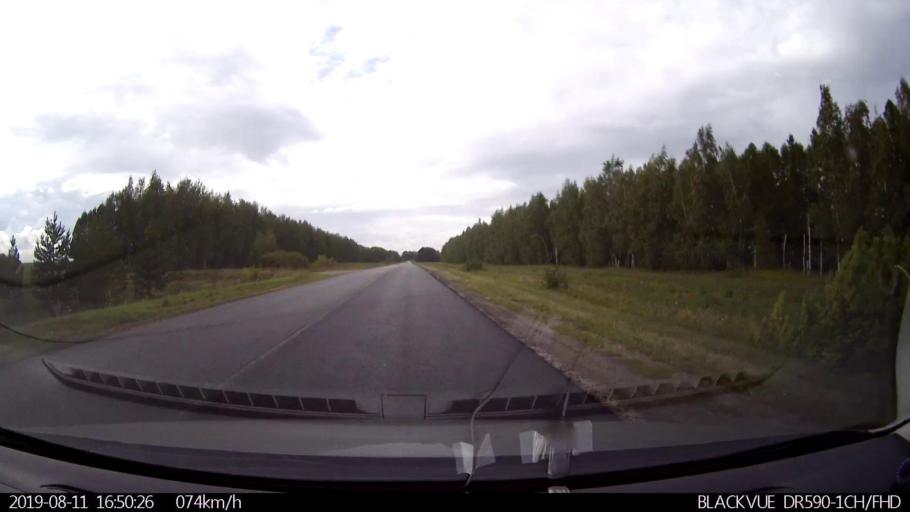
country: RU
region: Ulyanovsk
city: Mayna
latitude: 54.2288
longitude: 47.6874
